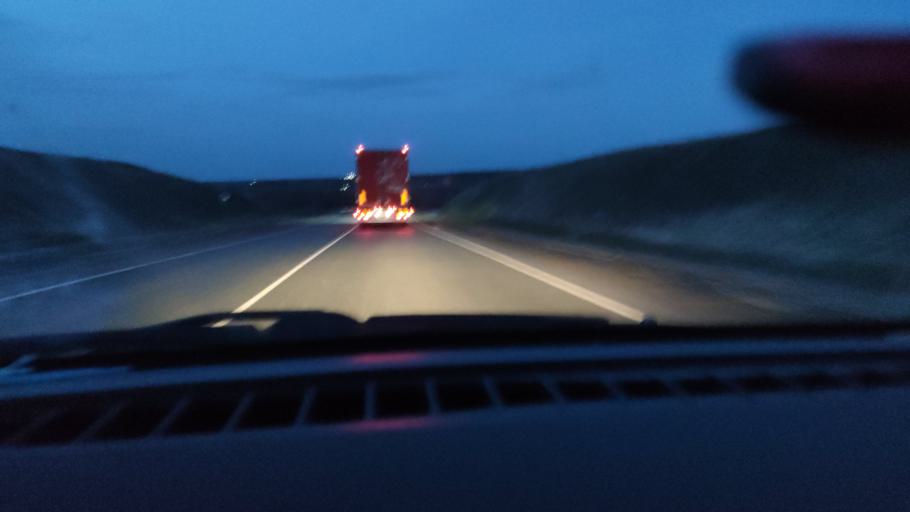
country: RU
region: Saratov
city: Sennoy
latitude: 52.1406
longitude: 46.8878
